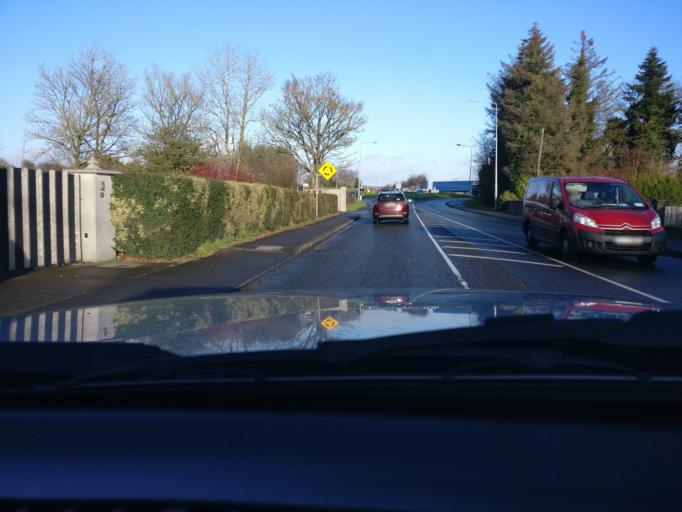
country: IE
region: Leinster
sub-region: An Iarmhi
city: An Muileann gCearr
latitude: 53.5407
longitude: -7.3417
